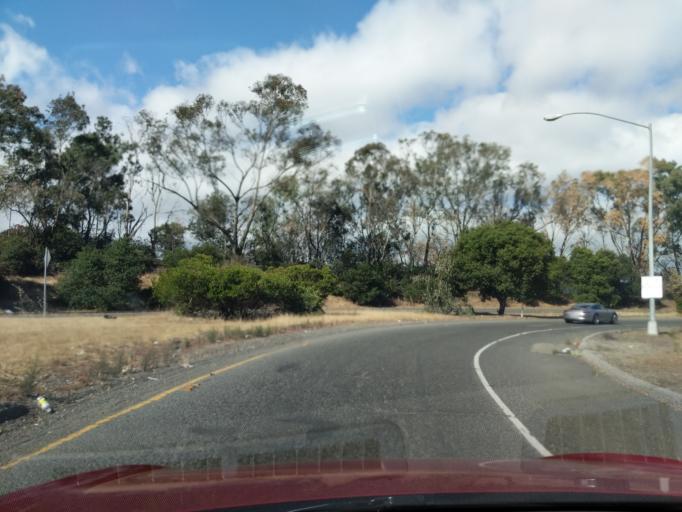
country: US
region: California
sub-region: San Mateo County
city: Ladera
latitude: 37.4084
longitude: -122.1952
